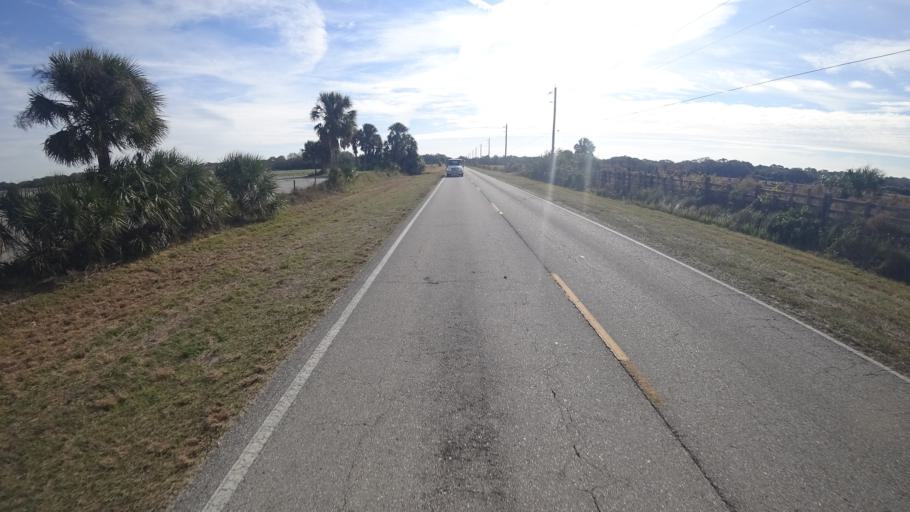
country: US
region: Florida
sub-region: Manatee County
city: Ellenton
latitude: 27.5971
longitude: -82.4582
